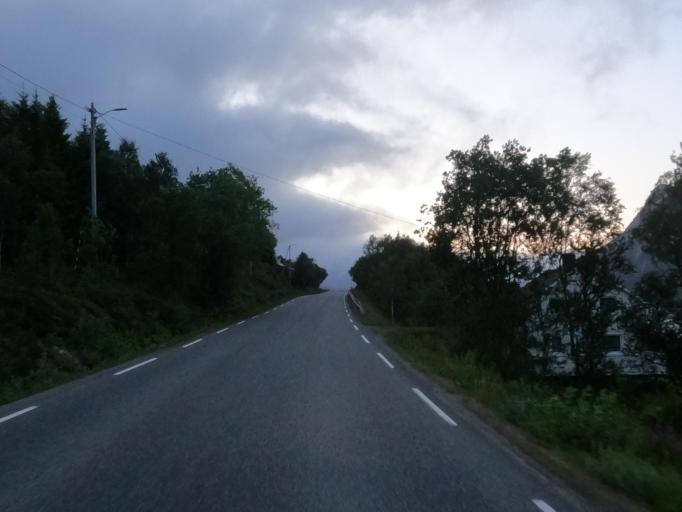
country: NO
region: Nordland
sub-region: Lodingen
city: Lodingen
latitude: 68.5772
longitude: 15.7932
